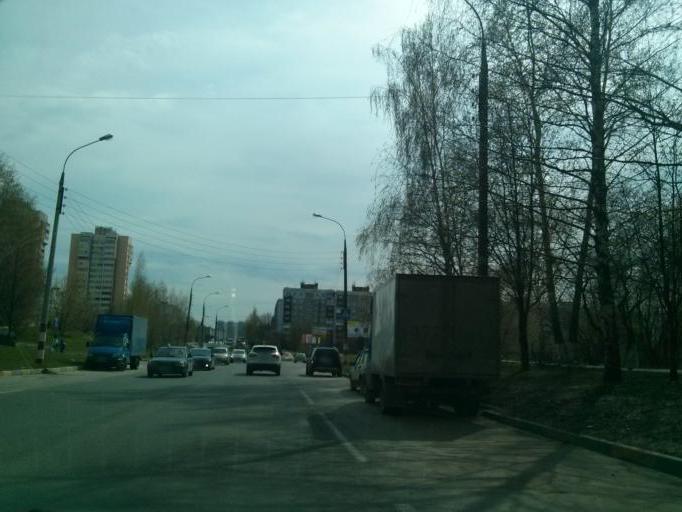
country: RU
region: Nizjnij Novgorod
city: Afonino
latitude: 56.2968
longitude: 44.0678
